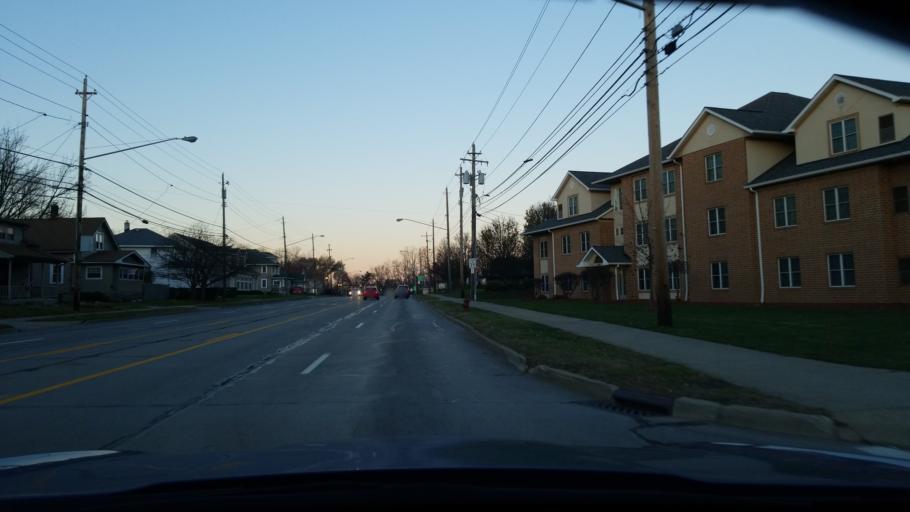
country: US
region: Ohio
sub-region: Cuyahoga County
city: Berea
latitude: 41.3729
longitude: -81.8580
